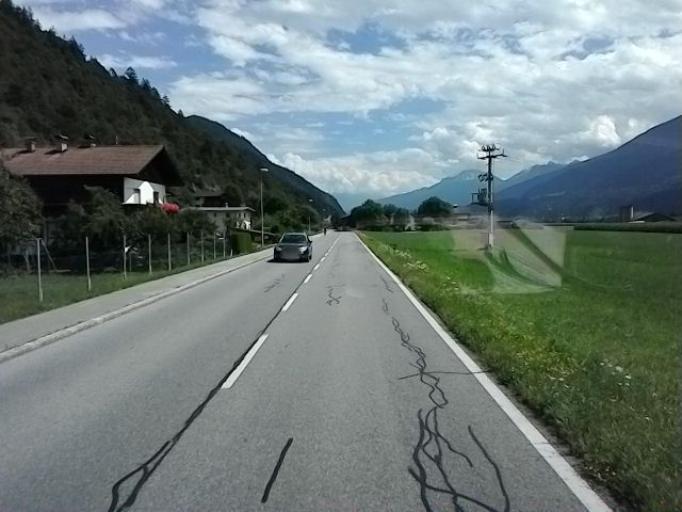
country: AT
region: Tyrol
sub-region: Politischer Bezirk Innsbruck Land
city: Pettnau
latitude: 47.3030
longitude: 11.1309
